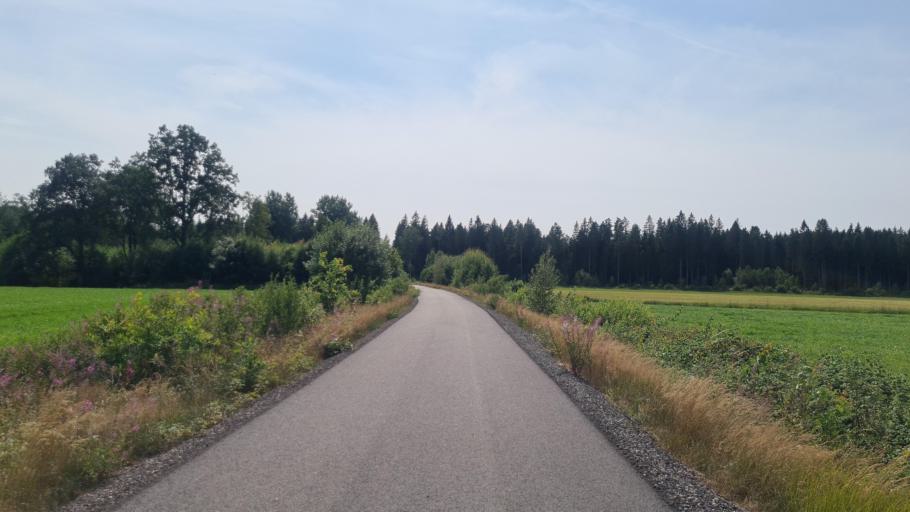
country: SE
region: Kronoberg
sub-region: Ljungby Kommun
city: Ljungby
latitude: 56.8662
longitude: 13.9774
